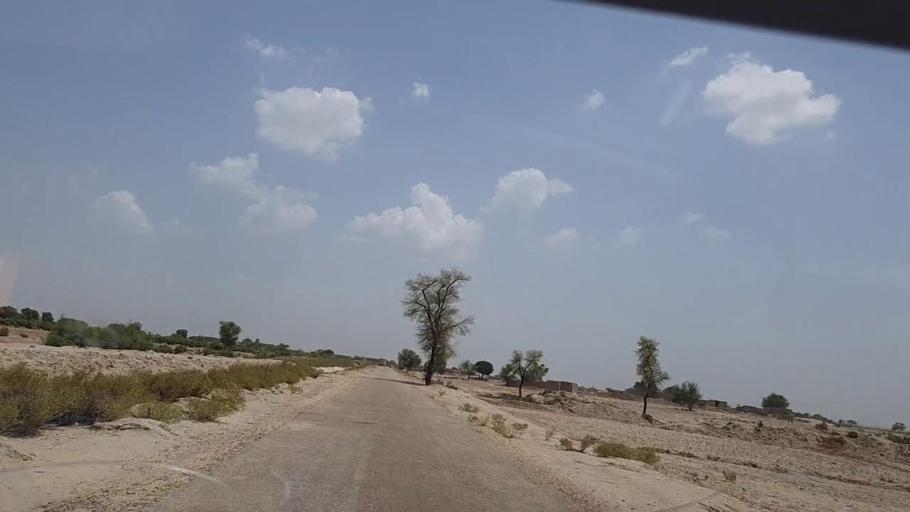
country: PK
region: Sindh
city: Bhan
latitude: 26.5256
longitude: 67.6343
